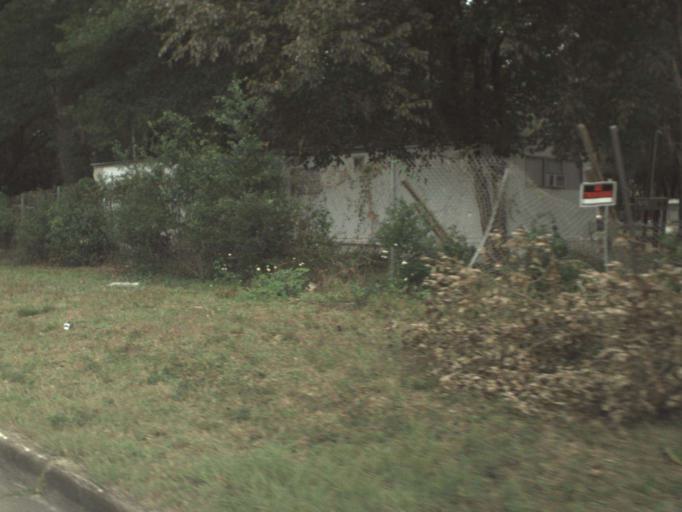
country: US
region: Florida
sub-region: Escambia County
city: West Pensacola
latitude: 30.4352
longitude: -87.2674
